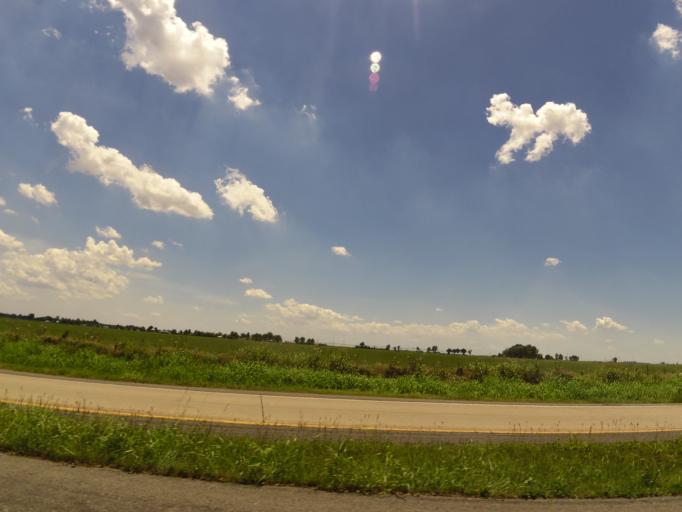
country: US
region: Missouri
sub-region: Pemiscot County
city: Caruthersville
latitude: 36.1741
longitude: -89.6916
